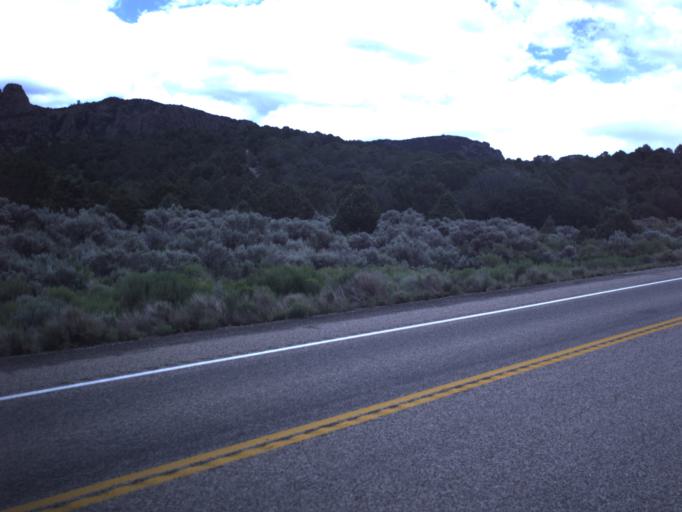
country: US
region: Utah
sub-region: Garfield County
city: Panguitch
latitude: 38.0412
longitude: -112.5513
